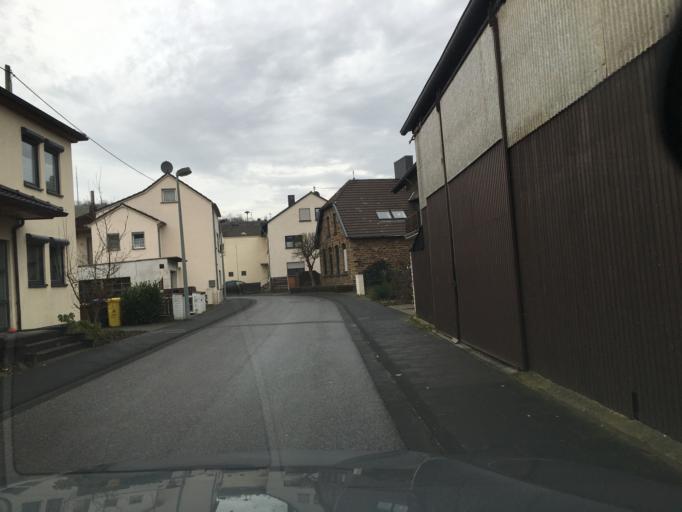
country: DE
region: Rheinland-Pfalz
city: Schalkenbach
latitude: 50.5500
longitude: 7.1646
